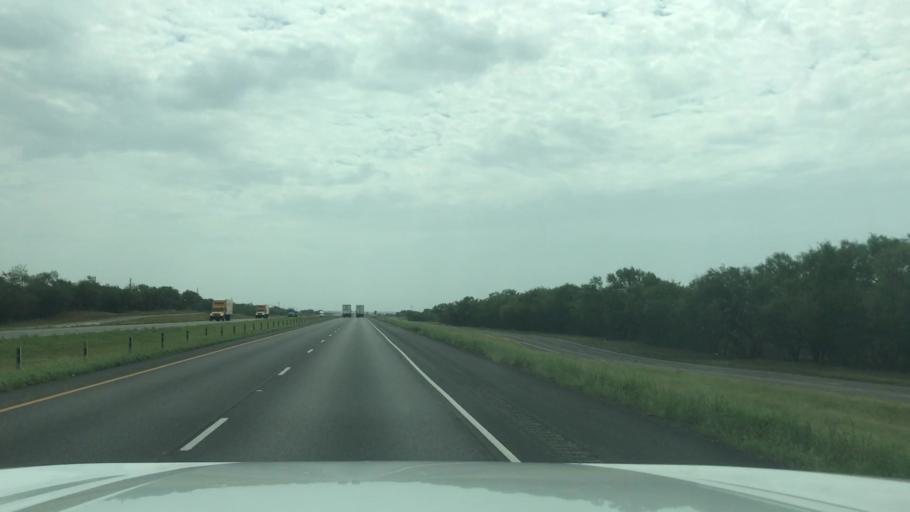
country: US
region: Texas
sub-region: Callahan County
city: Baird
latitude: 32.3872
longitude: -99.3106
